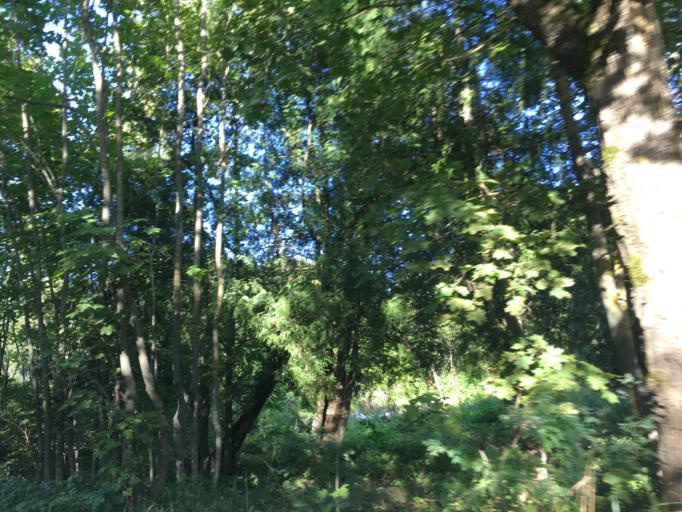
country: RU
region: Pskov
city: Izborsk
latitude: 57.7679
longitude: 27.9743
